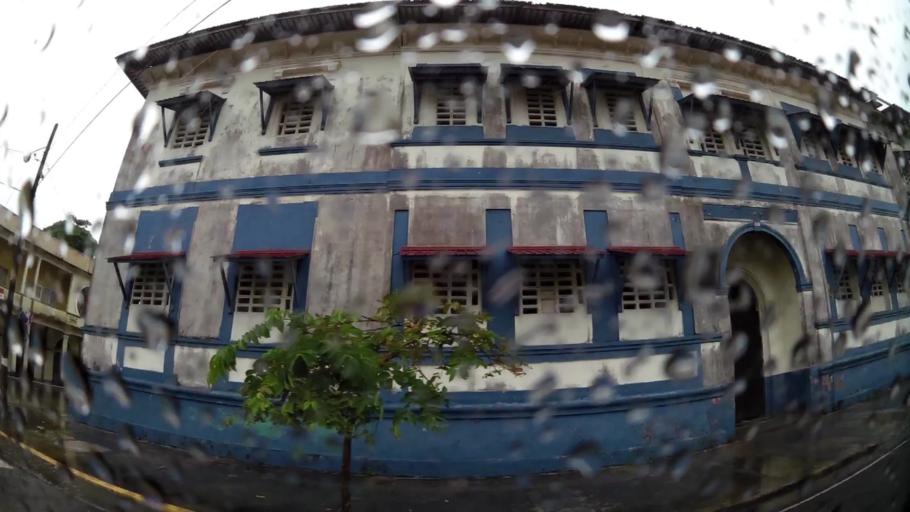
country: PA
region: Colon
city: Colon
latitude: 9.3638
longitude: -79.9059
